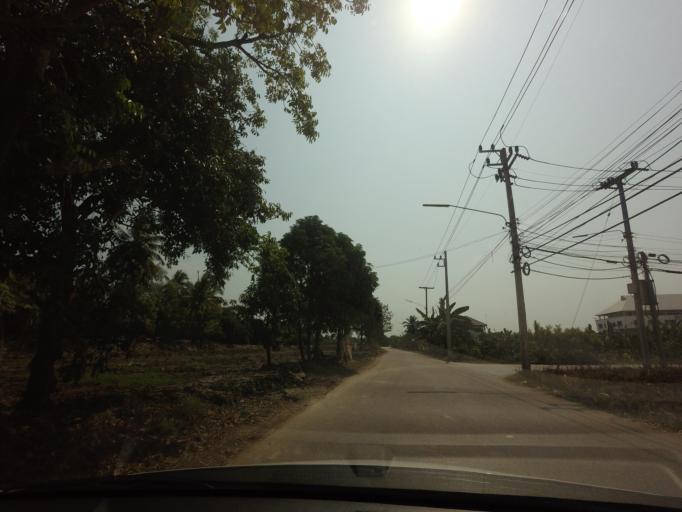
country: TH
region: Nakhon Pathom
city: Sam Phran
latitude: 13.7466
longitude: 100.2636
